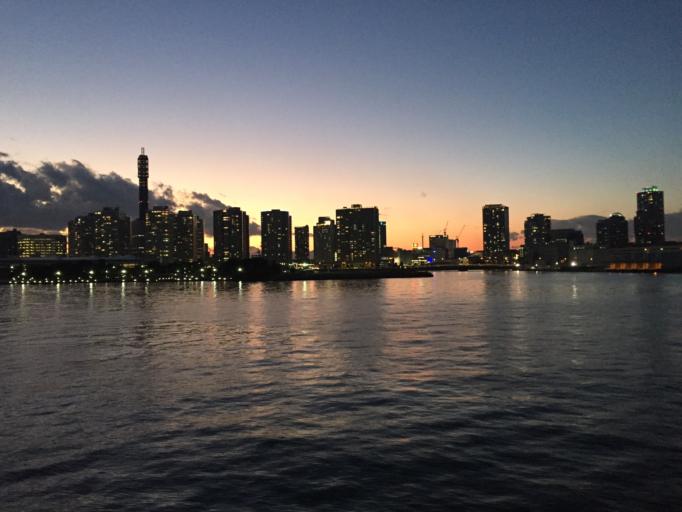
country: JP
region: Kanagawa
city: Yokohama
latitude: 35.4631
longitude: 139.6429
